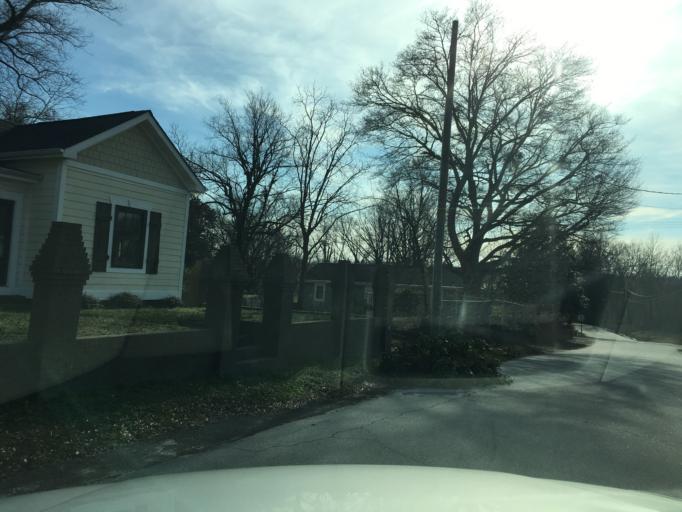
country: US
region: South Carolina
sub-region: Greenville County
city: Greenville
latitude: 34.8557
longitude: -82.4118
